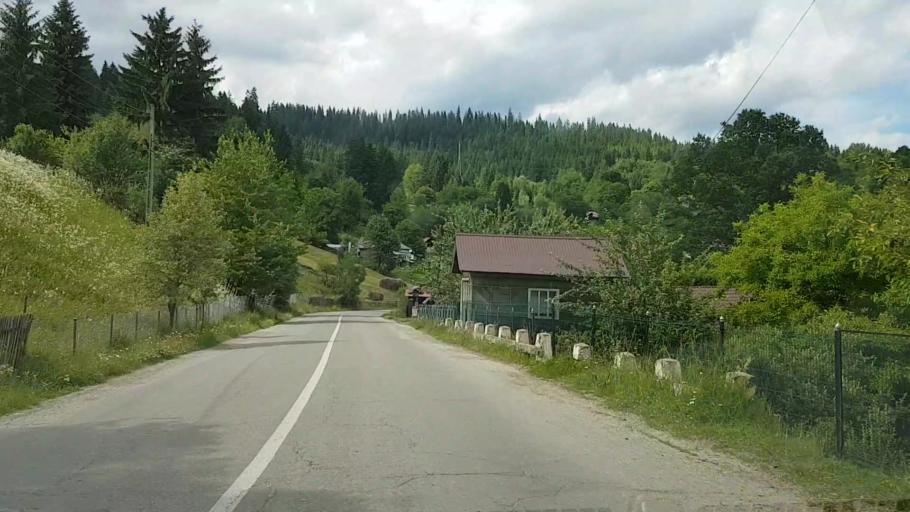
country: RO
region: Neamt
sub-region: Comuna Hangu
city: Hangu
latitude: 47.0518
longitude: 26.0244
